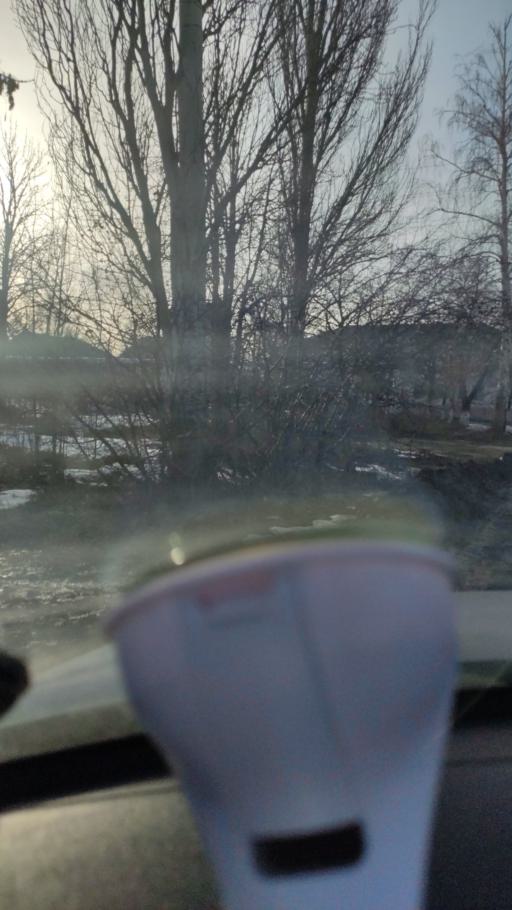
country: RU
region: Samara
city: Smyshlyayevka
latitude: 53.2481
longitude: 50.4846
